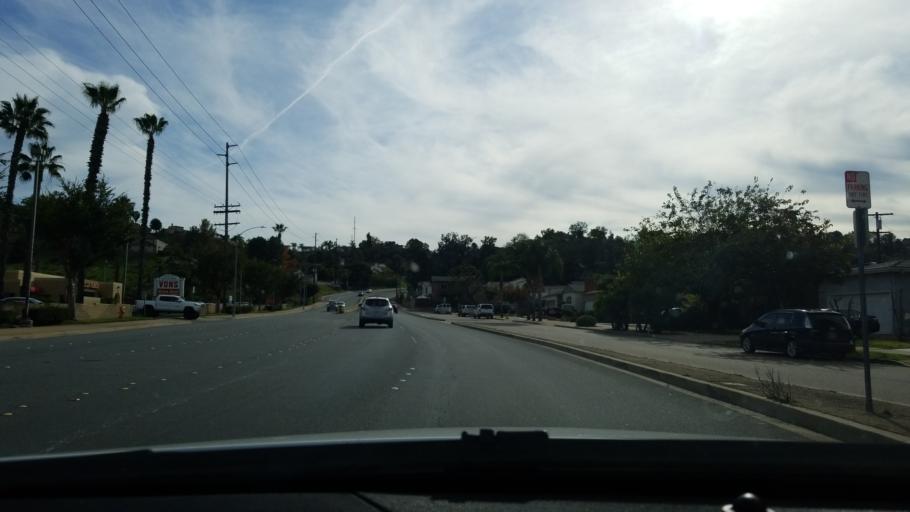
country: US
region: California
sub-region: San Diego County
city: El Cajon
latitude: 32.7798
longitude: -116.9581
